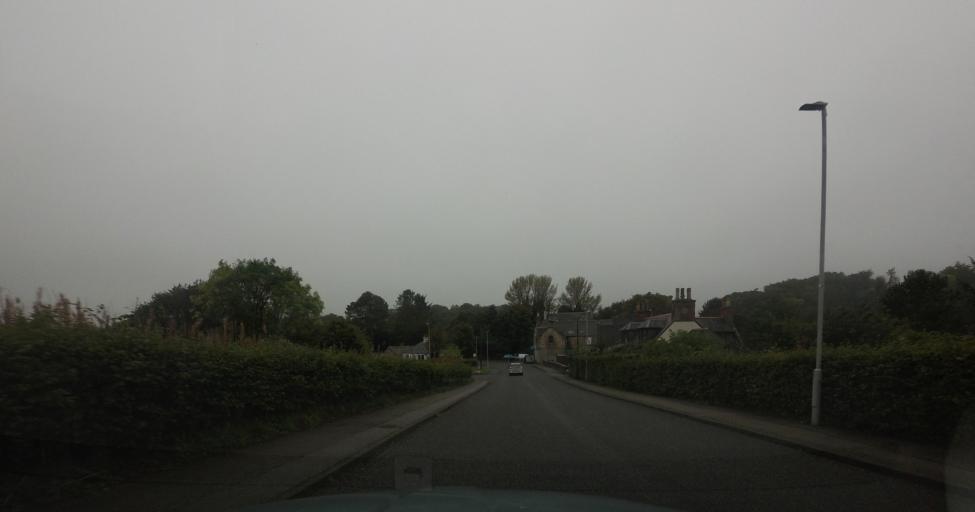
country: GB
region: Scotland
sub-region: Aberdeenshire
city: Oldmeldrum
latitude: 57.4301
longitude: -2.3947
